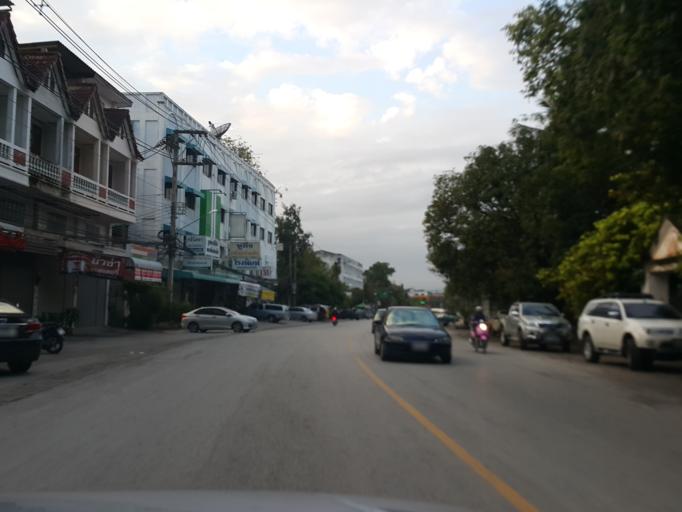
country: TH
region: Lampang
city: Lampang
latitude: 18.2841
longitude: 99.5050
